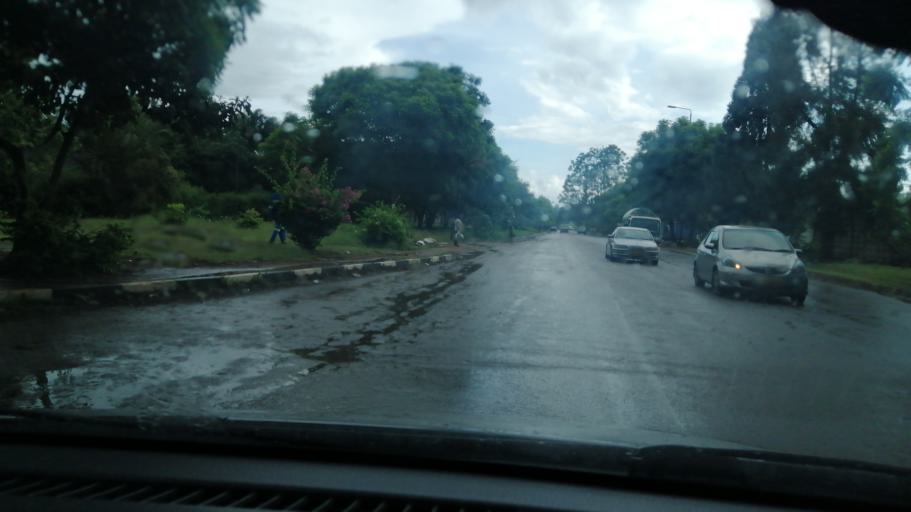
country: ZW
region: Harare
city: Harare
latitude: -17.7634
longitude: 31.0700
